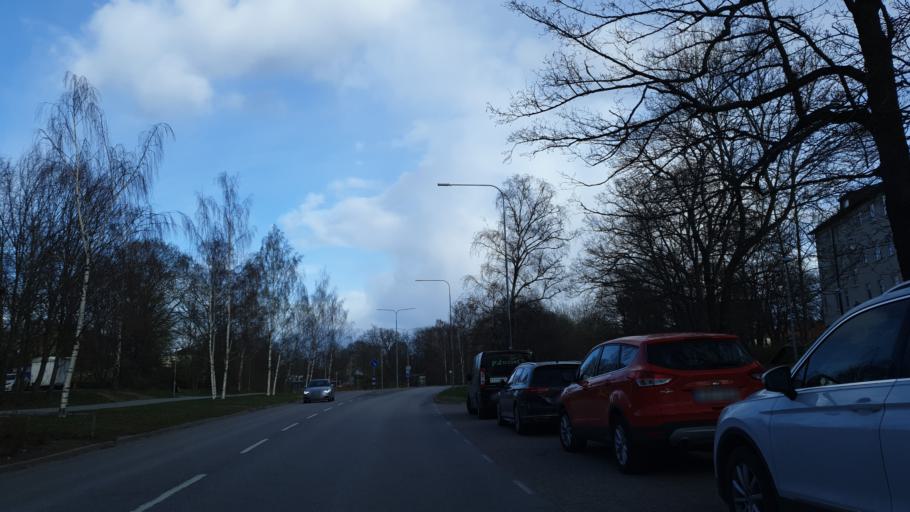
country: SE
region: Stockholm
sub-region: Lidingo
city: Lidingoe
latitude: 59.3671
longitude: 18.1501
